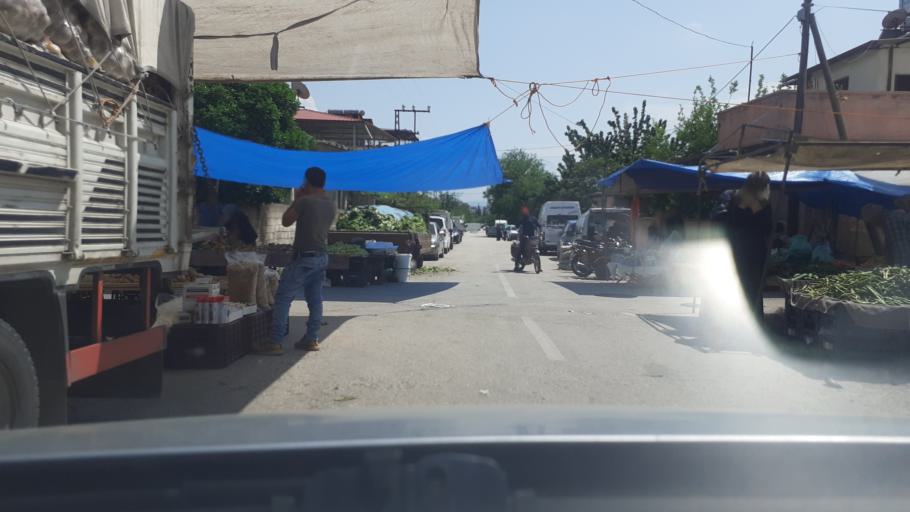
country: TR
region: Hatay
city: Kirikhan
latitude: 36.4925
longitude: 36.3540
